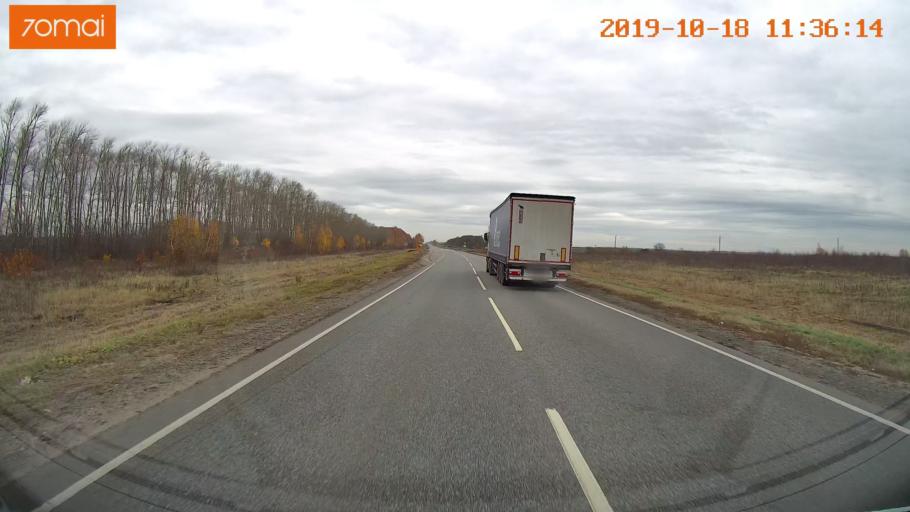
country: RU
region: Rjazan
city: Oktyabr'skiy
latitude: 54.1387
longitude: 38.8019
